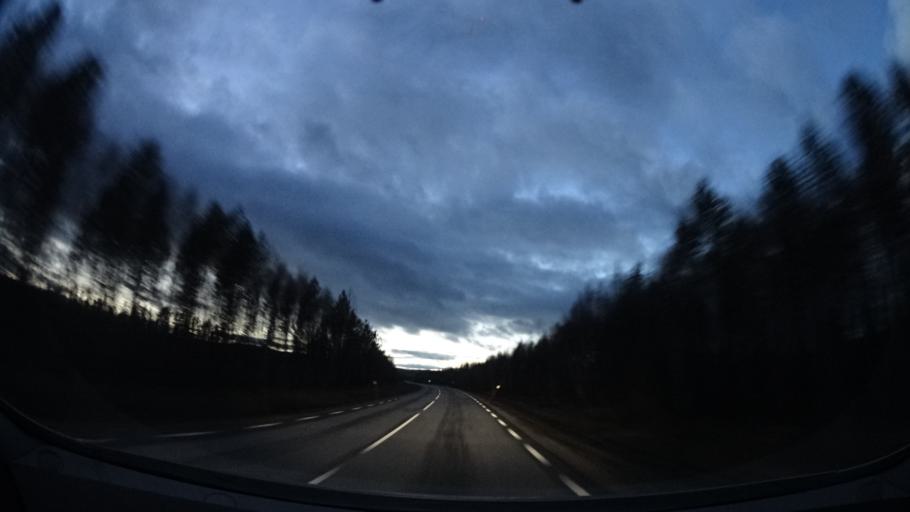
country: SE
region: Vaesterbotten
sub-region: Dorotea Kommun
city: Dorotea
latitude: 64.2409
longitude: 16.7332
